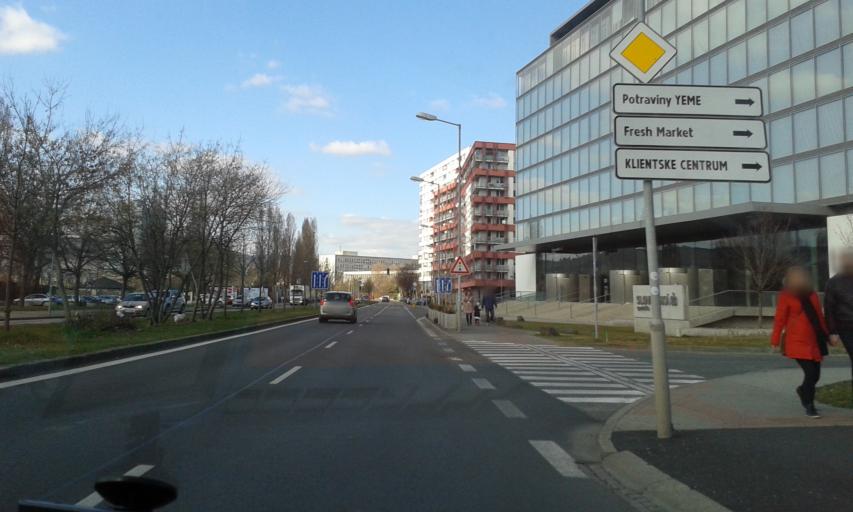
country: SK
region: Bratislavsky
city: Bratislava
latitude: 48.1665
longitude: 17.1500
